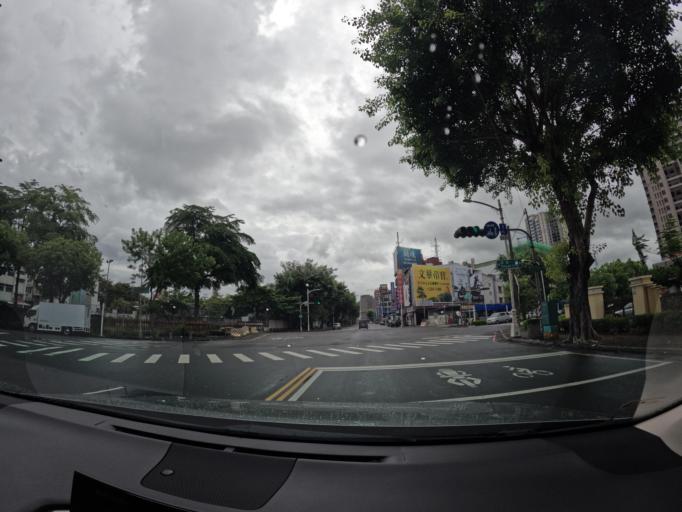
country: TW
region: Kaohsiung
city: Kaohsiung
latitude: 22.6338
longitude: 120.3199
